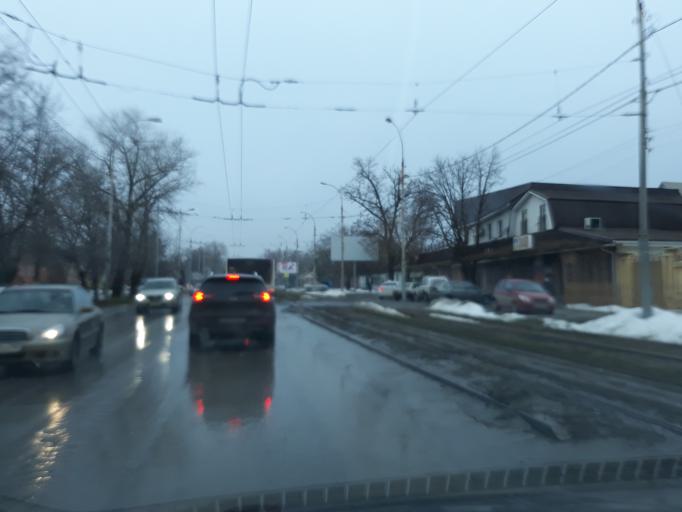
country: RU
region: Rostov
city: Taganrog
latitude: 47.2313
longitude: 38.9180
